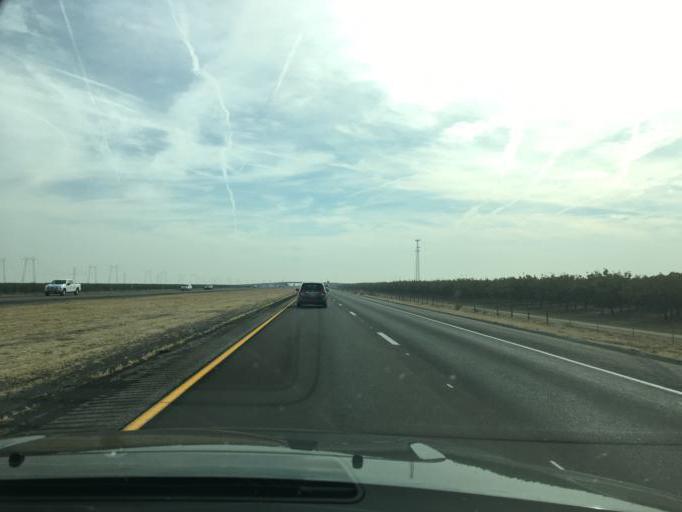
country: US
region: California
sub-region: Kings County
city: Kettleman City
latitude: 35.8825
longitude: -119.8595
